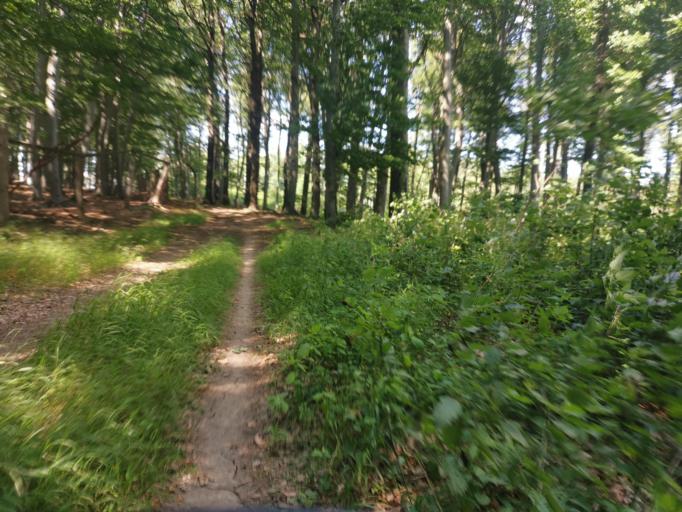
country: CZ
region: South Moravian
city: Knezdub
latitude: 48.8190
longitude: 17.4026
